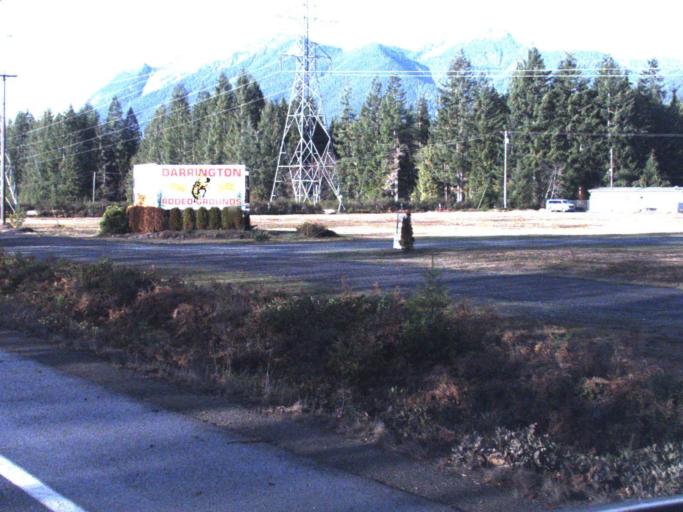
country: US
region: Washington
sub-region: Snohomish County
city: Darrington
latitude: 48.2729
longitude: -121.6605
